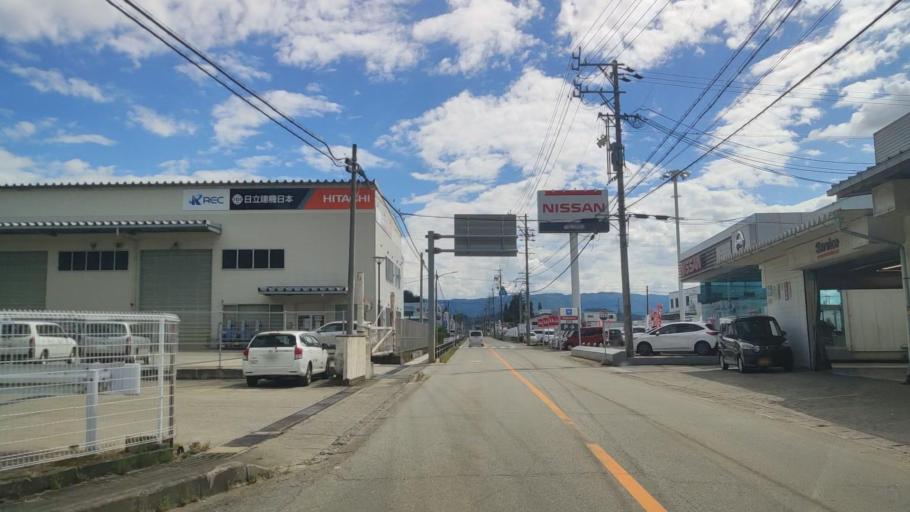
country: JP
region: Gifu
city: Takayama
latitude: 36.1693
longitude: 137.2466
